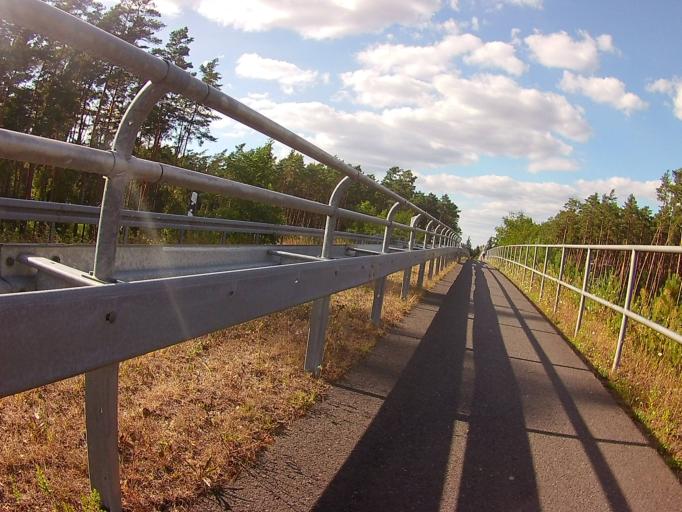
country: DE
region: Berlin
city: Bohnsdorf
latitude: 52.3889
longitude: 13.5869
